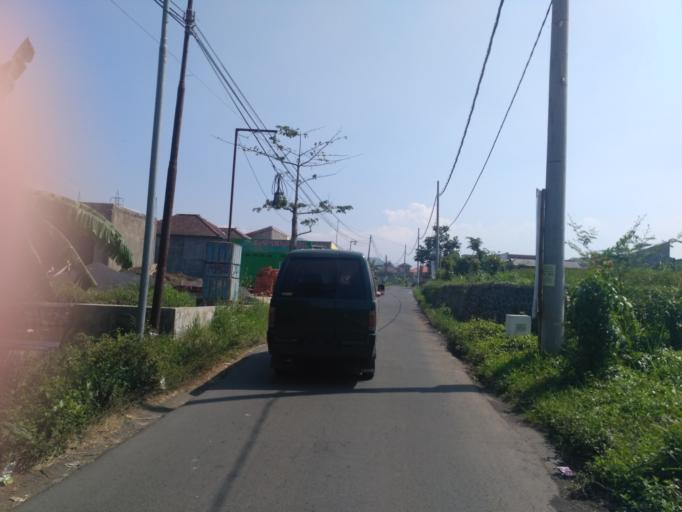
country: ID
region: East Java
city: Batu
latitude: -7.9080
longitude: 112.5858
